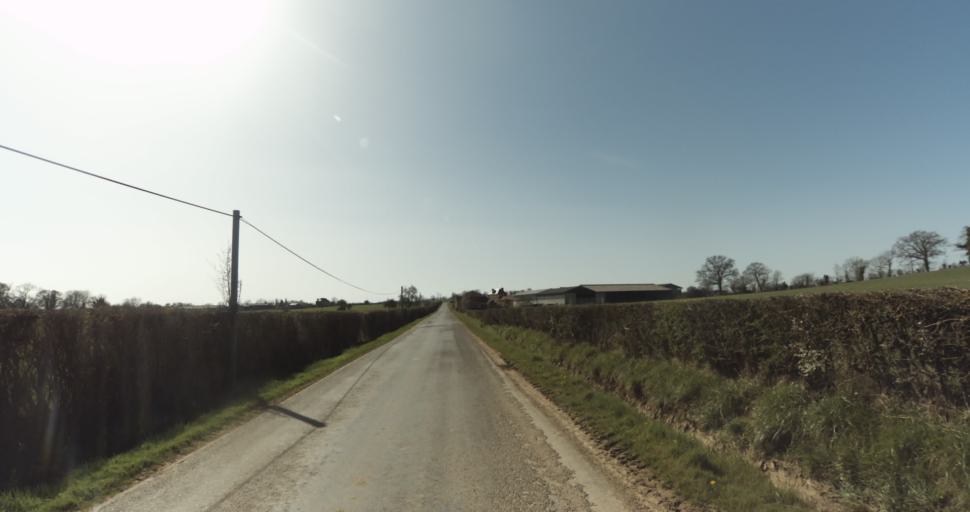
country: FR
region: Lower Normandy
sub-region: Departement du Calvados
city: Saint-Pierre-sur-Dives
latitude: 48.9402
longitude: 0.0160
